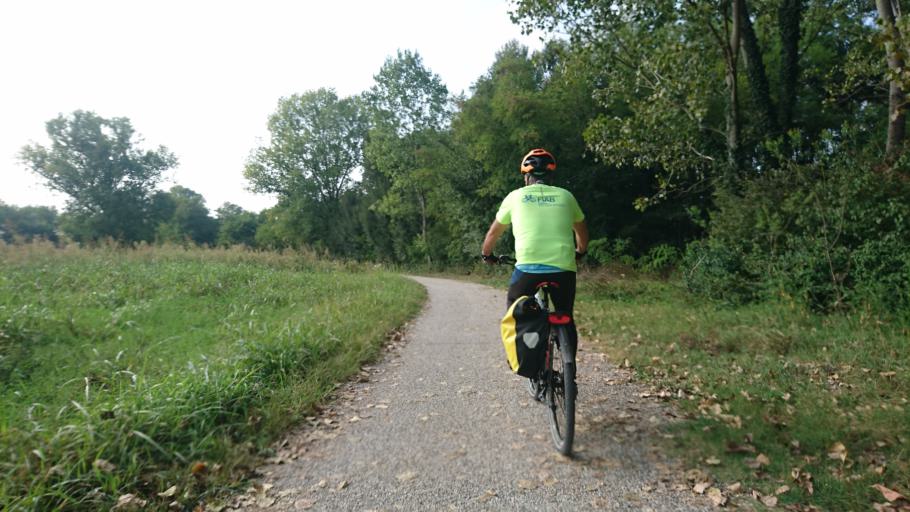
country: IT
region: Veneto
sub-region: Provincia di Padova
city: Grantorto
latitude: 45.5918
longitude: 11.7617
